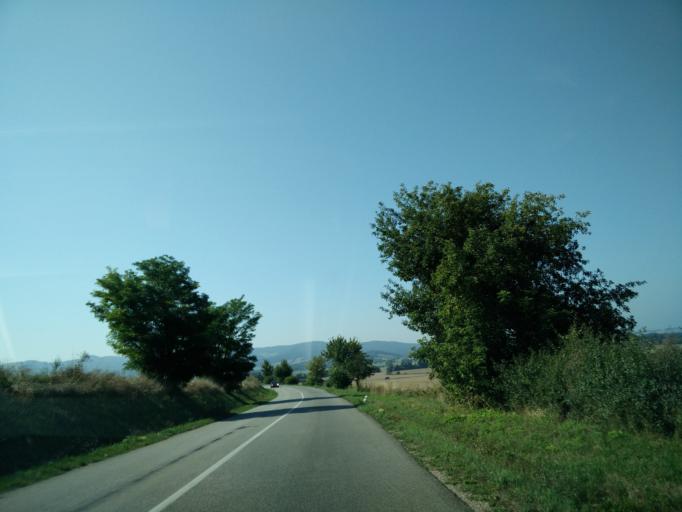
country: SK
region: Nitriansky
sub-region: Okres Nitra
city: Nitra
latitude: 48.4158
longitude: 18.1161
